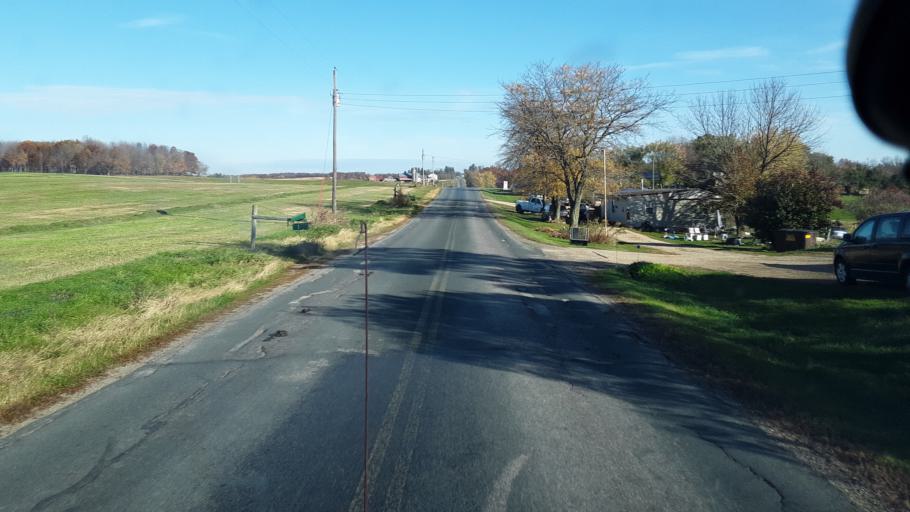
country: US
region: Wisconsin
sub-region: Vernon County
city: Hillsboro
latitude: 43.7876
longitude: -90.4433
